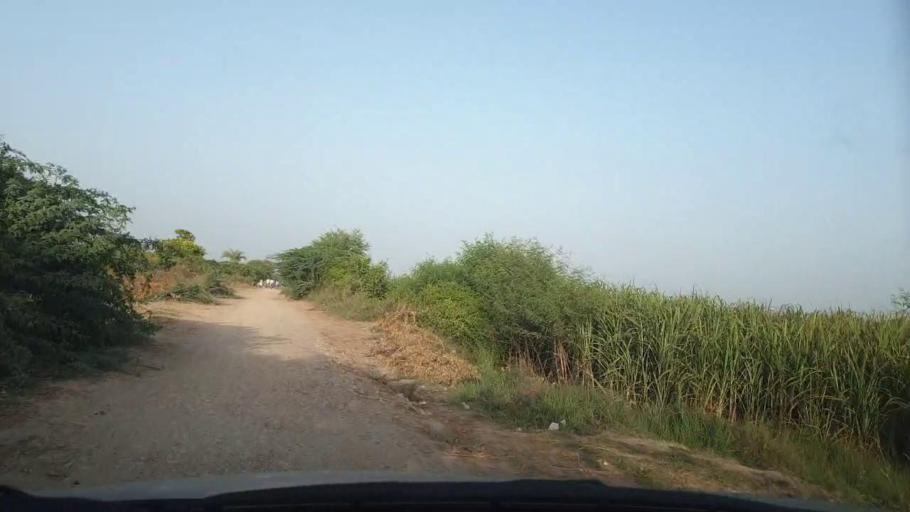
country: PK
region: Sindh
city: Talhar
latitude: 24.9290
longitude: 68.8209
